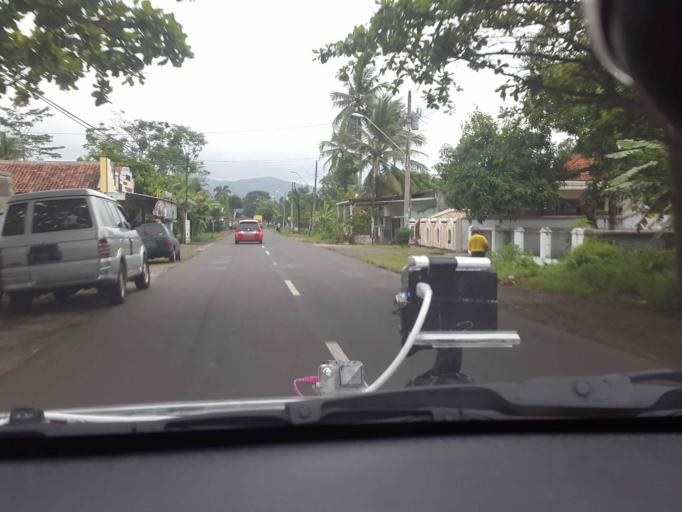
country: ID
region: Central Java
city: Banyumas
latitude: -7.5173
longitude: 109.3000
